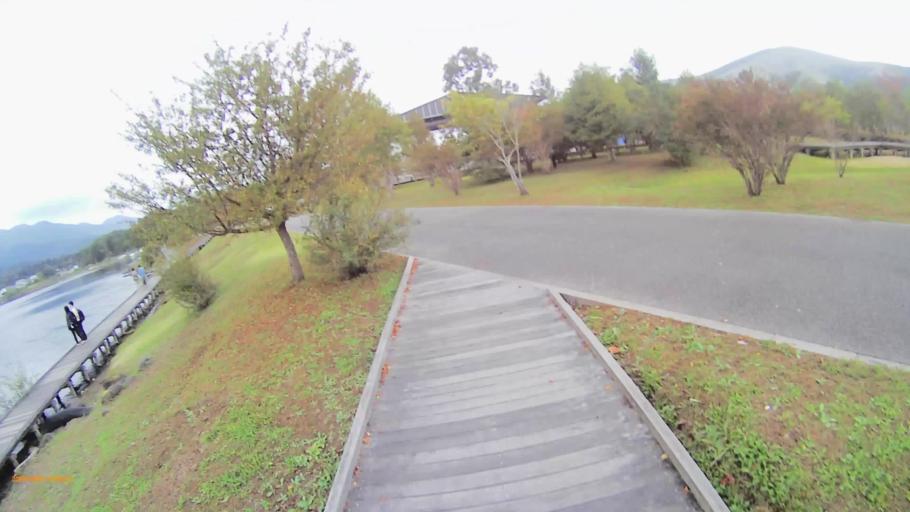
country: JP
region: Shizuoka
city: Gotemba
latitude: 35.4202
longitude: 138.9001
